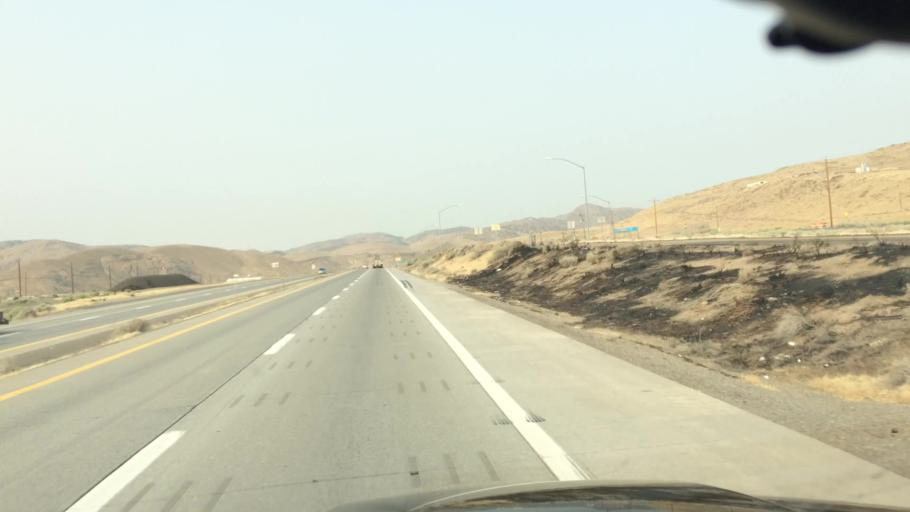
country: US
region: Nevada
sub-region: Washoe County
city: Sparks
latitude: 39.5264
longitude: -119.6198
